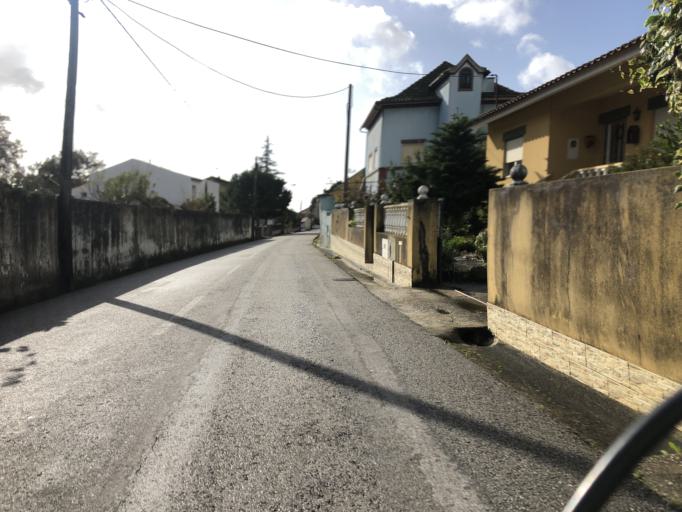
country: PT
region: Aveiro
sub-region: Estarreja
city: Beduido
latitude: 40.7648
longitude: -8.5563
